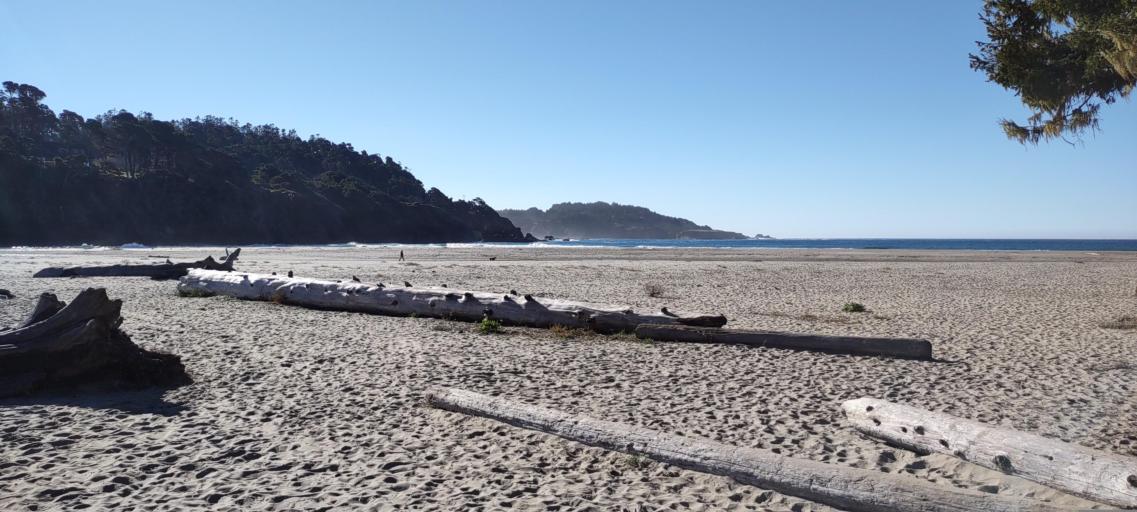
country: US
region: California
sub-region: Mendocino County
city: Fort Bragg
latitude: 39.3040
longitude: -123.7950
